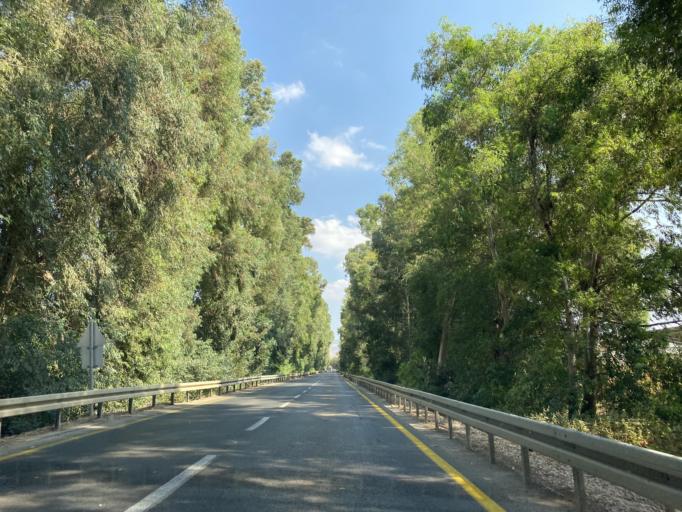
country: IL
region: Northern District
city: Qiryat Shemona
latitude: 33.1678
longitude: 35.5857
